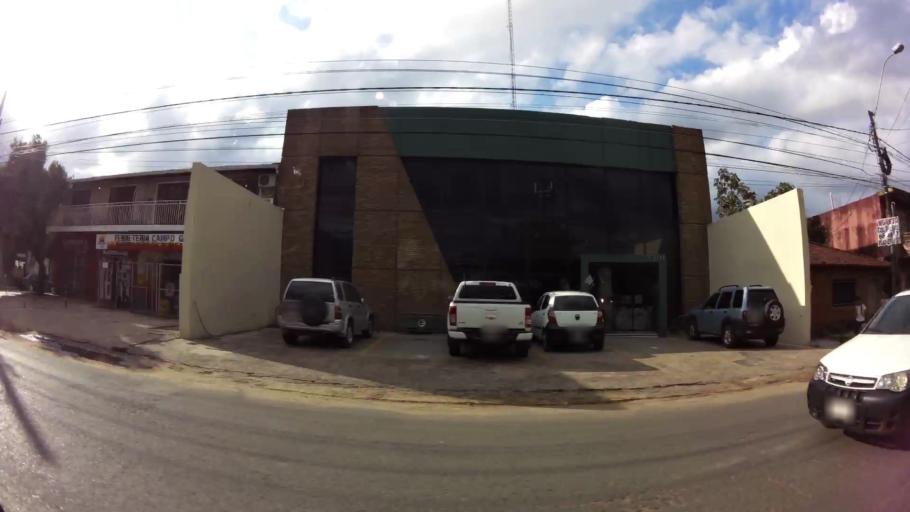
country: PY
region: Central
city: Fernando de la Mora
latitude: -25.2775
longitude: -57.5531
